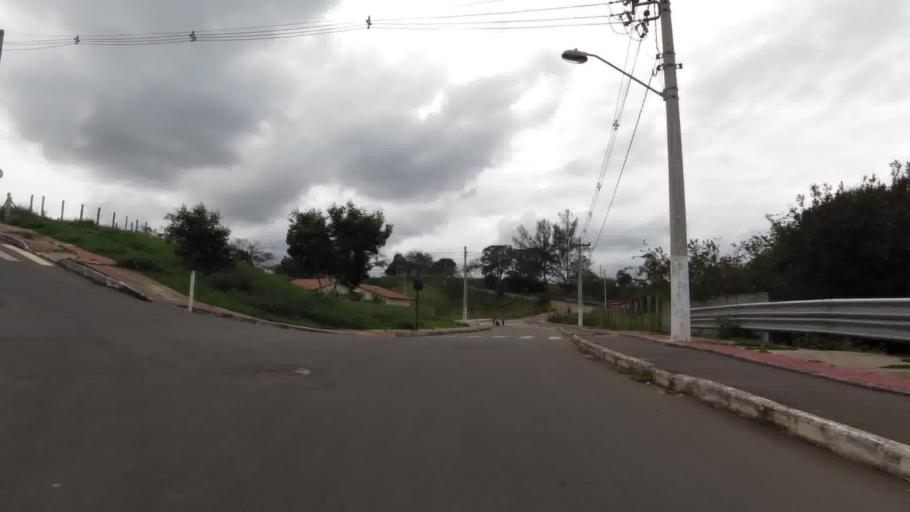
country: BR
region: Espirito Santo
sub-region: Piuma
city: Piuma
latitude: -20.8023
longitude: -40.6471
